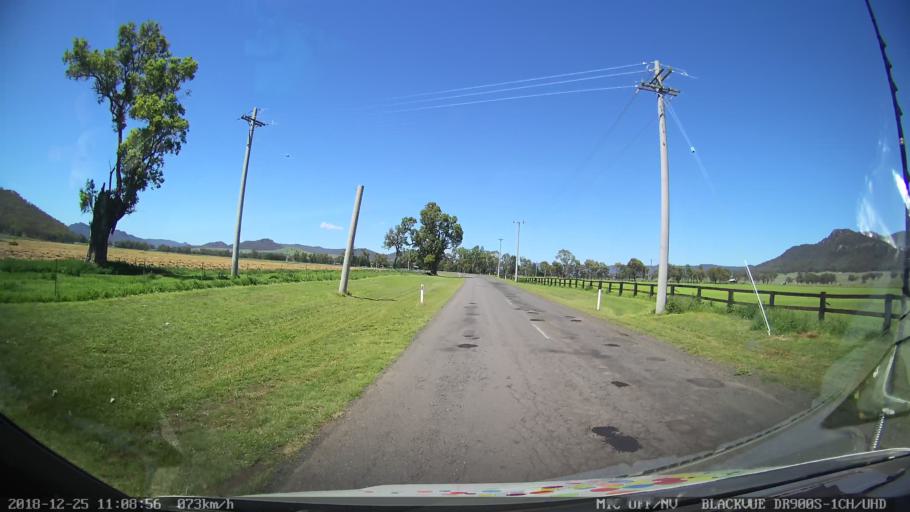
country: AU
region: New South Wales
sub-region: Upper Hunter Shire
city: Merriwa
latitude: -32.4064
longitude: 150.1208
